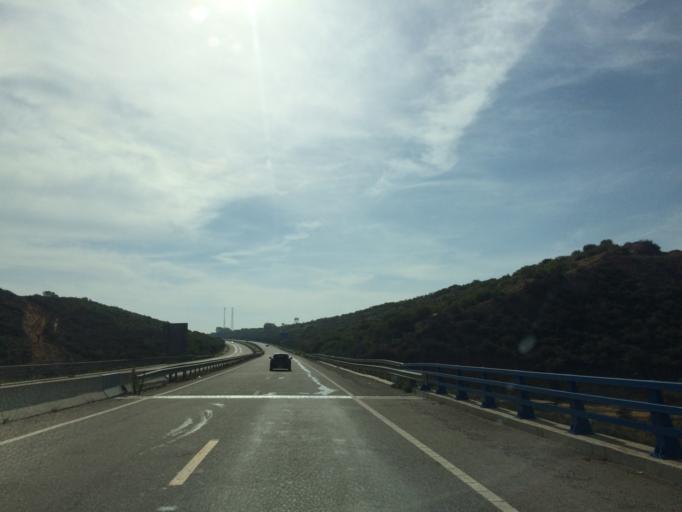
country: MA
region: Tanger-Tetouan
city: Asilah
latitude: 35.4610
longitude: -6.0146
